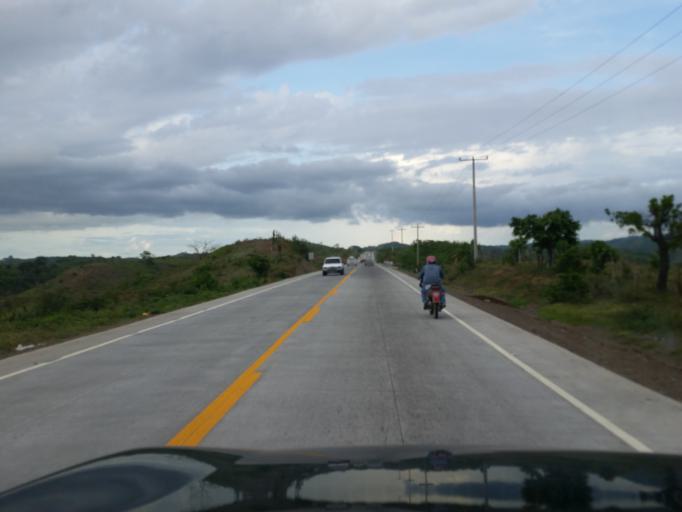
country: NI
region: Managua
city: Carlos Fonseca Amador
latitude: 12.0689
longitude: -86.4405
